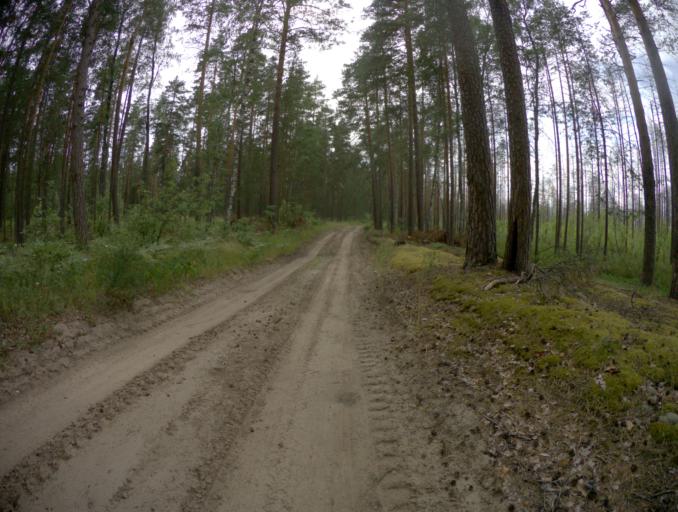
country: RU
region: Vladimir
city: Gorokhovets
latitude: 56.3001
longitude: 42.6792
